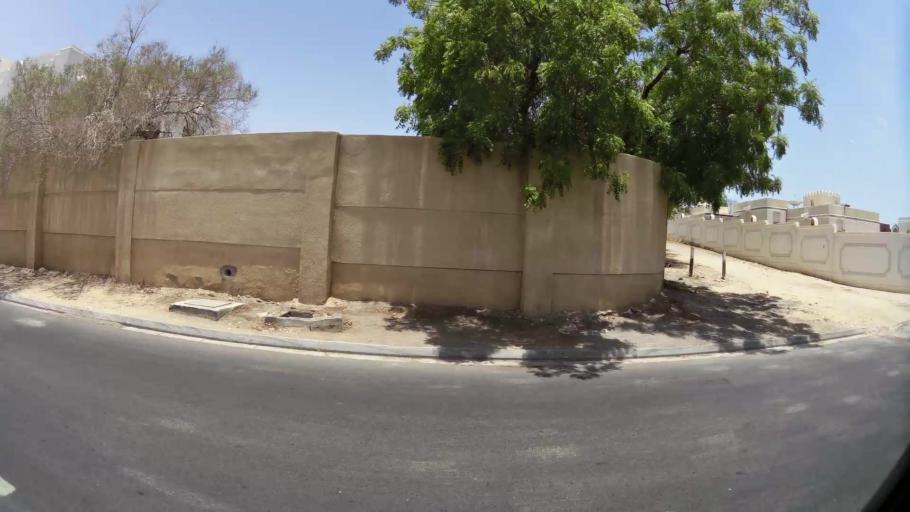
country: OM
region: Muhafazat Masqat
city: Bawshar
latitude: 23.6004
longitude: 58.4540
